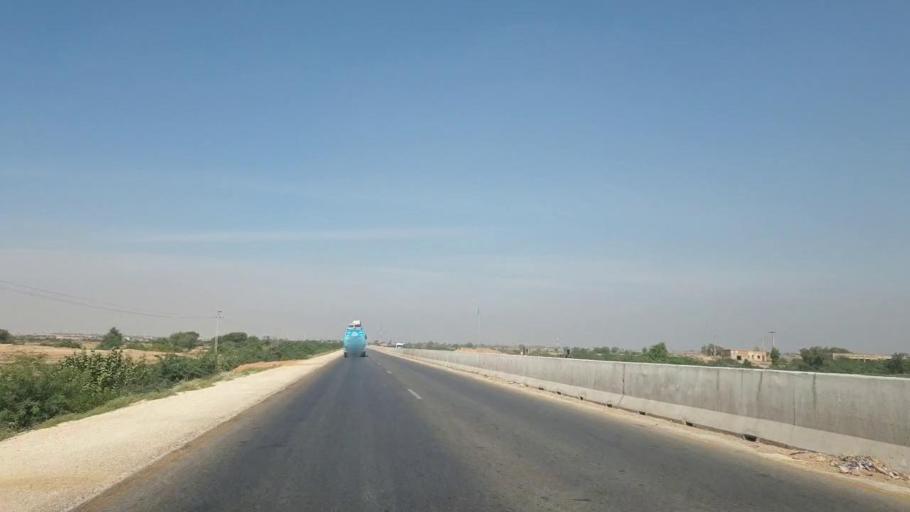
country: PK
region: Sindh
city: Matiari
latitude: 25.6336
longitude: 68.3017
